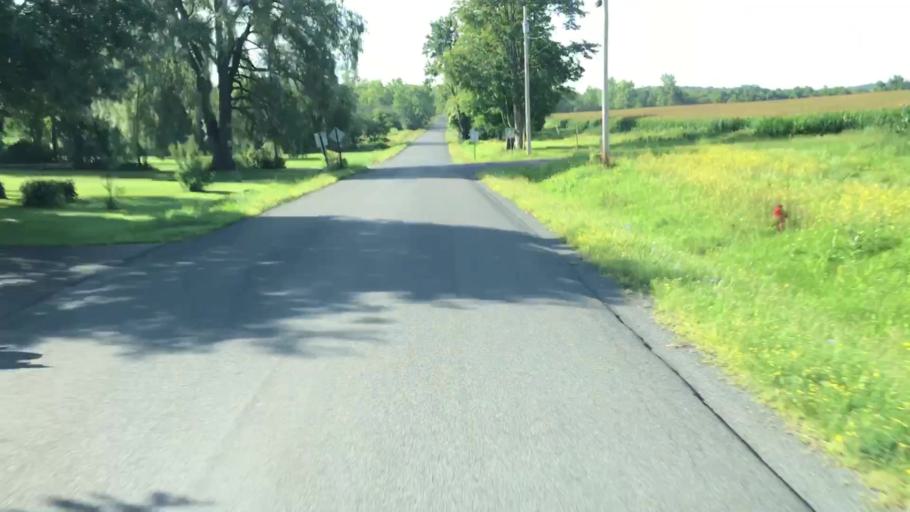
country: US
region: New York
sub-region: Cayuga County
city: Melrose Park
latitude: 42.9282
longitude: -76.5084
